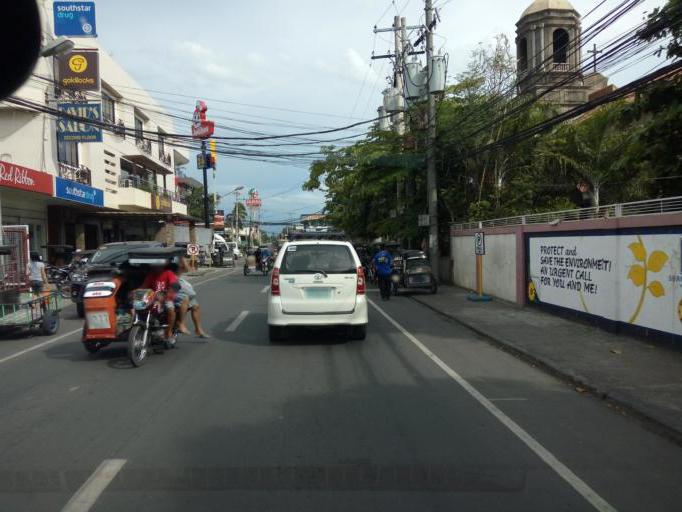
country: PH
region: Central Luzon
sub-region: Province of Nueva Ecija
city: Sibul
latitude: 15.7926
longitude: 120.9897
